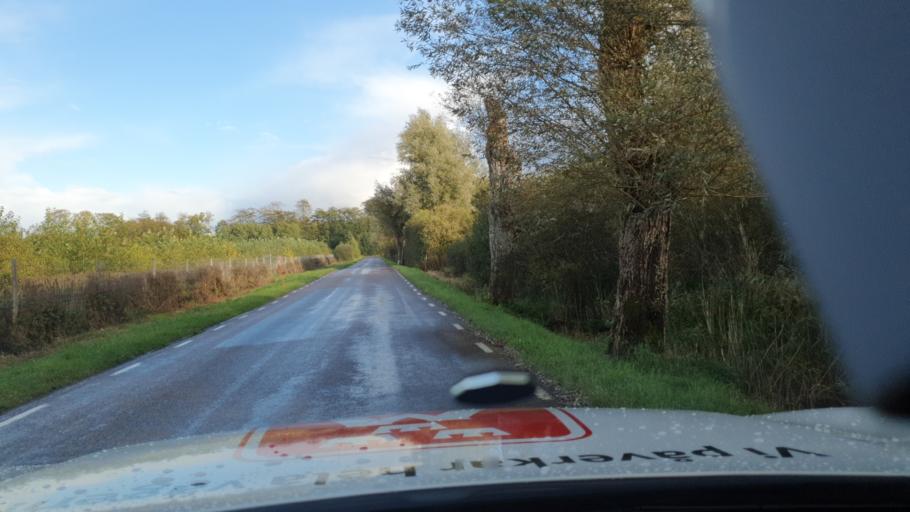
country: SE
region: Skane
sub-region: Svedala Kommun
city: Svedala
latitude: 55.5342
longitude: 13.1940
